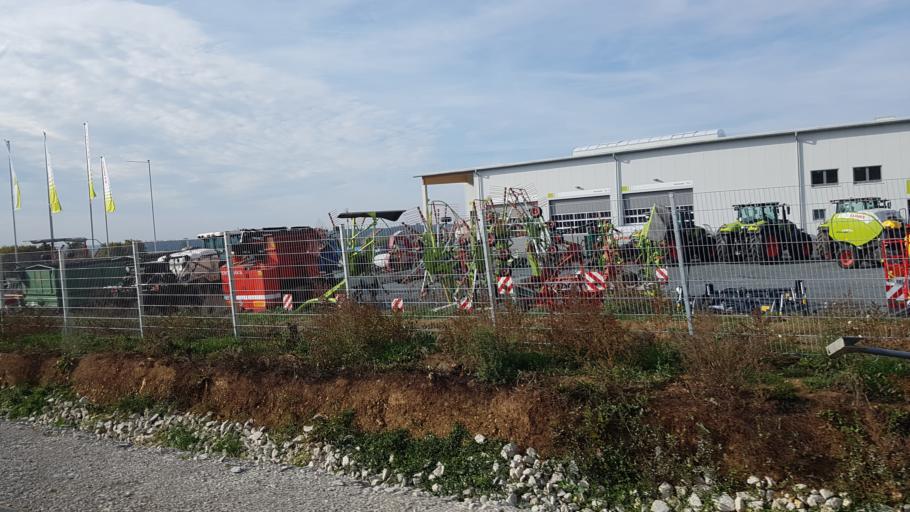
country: DE
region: Bavaria
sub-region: Upper Franconia
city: Hollfeld
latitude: 49.9483
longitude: 11.2850
